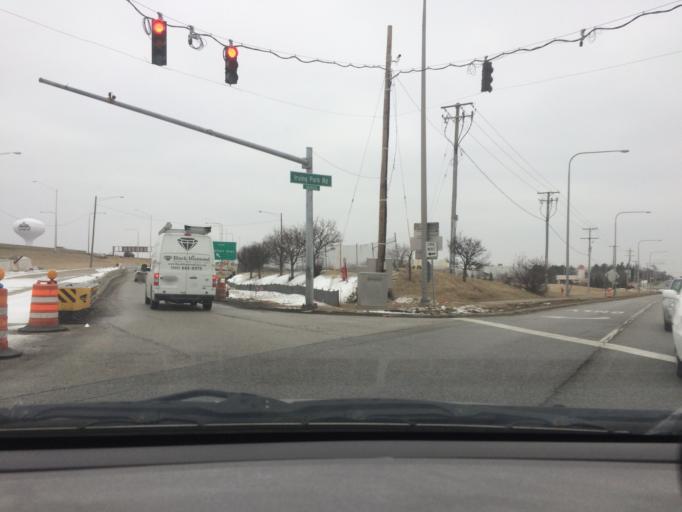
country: US
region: Illinois
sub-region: DuPage County
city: Hanover Park
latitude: 41.9960
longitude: -88.1142
